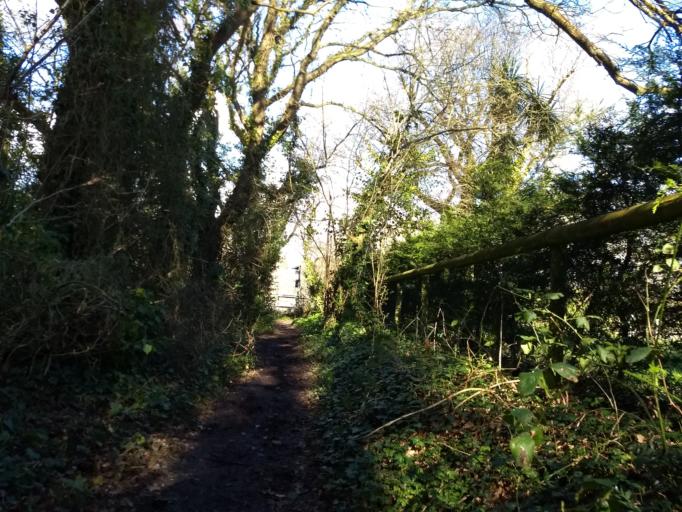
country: GB
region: England
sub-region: Isle of Wight
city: Ryde
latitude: 50.7307
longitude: -1.2161
